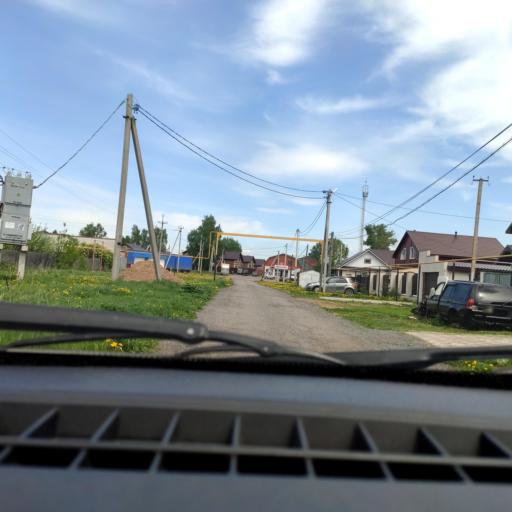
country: RU
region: Bashkortostan
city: Ufa
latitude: 54.5422
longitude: 55.9387
